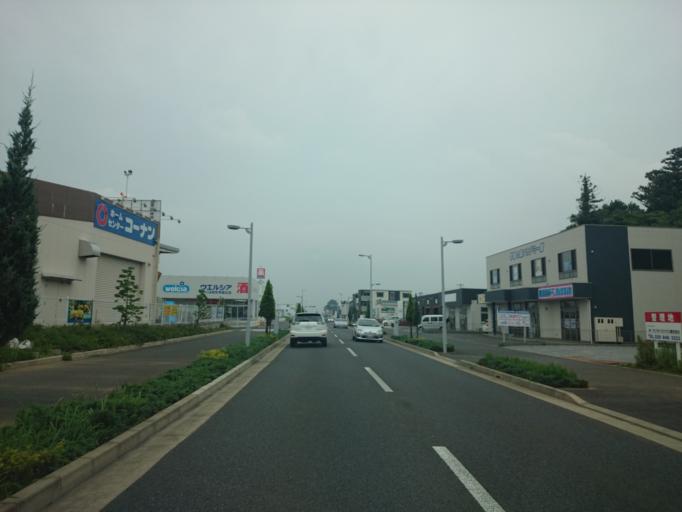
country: JP
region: Ibaraki
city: Tsukuba
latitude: 36.1004
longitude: 140.0762
